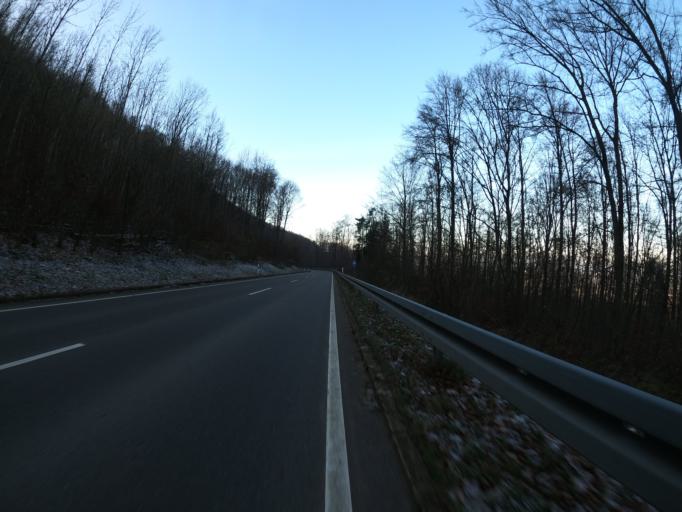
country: DE
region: Baden-Wuerttemberg
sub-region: Regierungsbezirk Stuttgart
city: Gammelshausen
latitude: 48.6297
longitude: 9.6693
